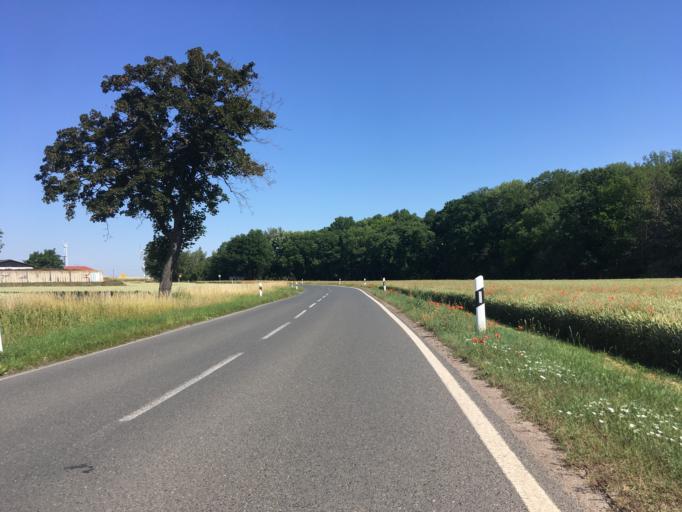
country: DE
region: Saxony-Anhalt
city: Baalberge
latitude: 51.7675
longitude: 11.8599
